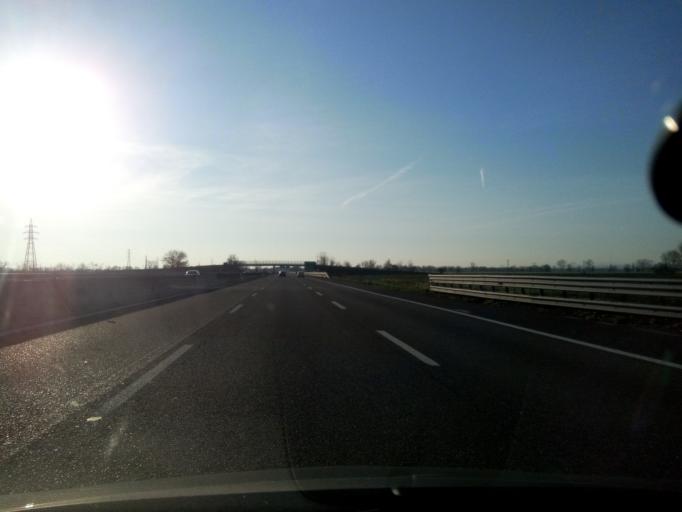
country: IT
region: Emilia-Romagna
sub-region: Provincia di Piacenza
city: Roveleto
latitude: 44.9705
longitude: 9.8868
